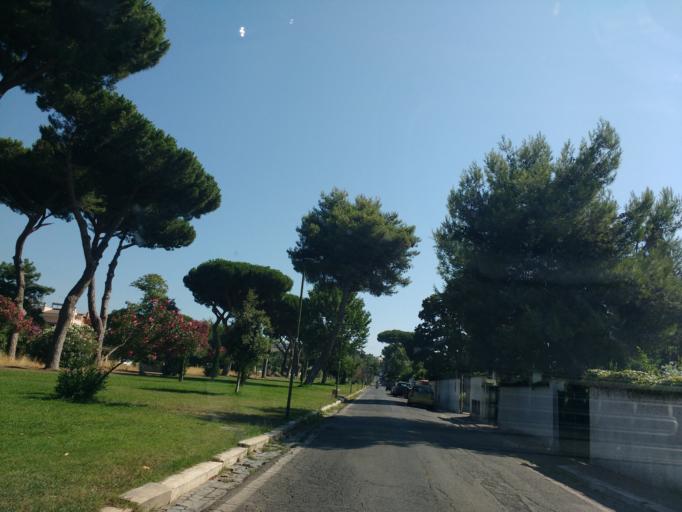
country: IT
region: Latium
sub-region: Citta metropolitana di Roma Capitale
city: Acilia-Castel Fusano-Ostia Antica
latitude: 41.7651
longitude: 12.3673
